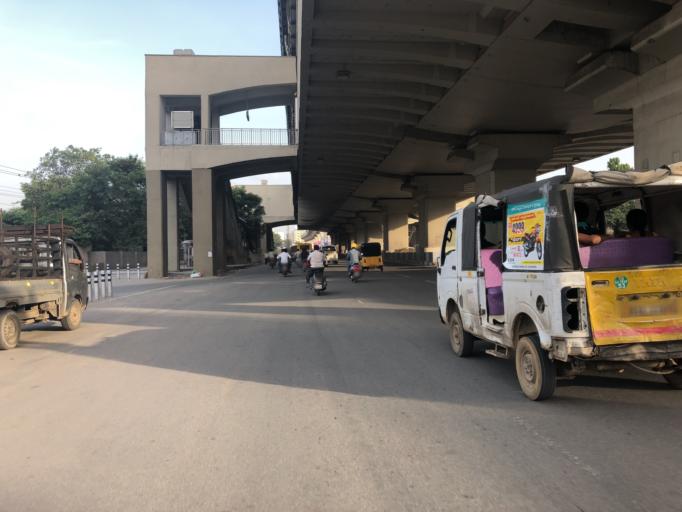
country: IN
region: Telangana
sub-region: Rangareddi
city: Kukatpalli
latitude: 17.4729
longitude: 78.4255
